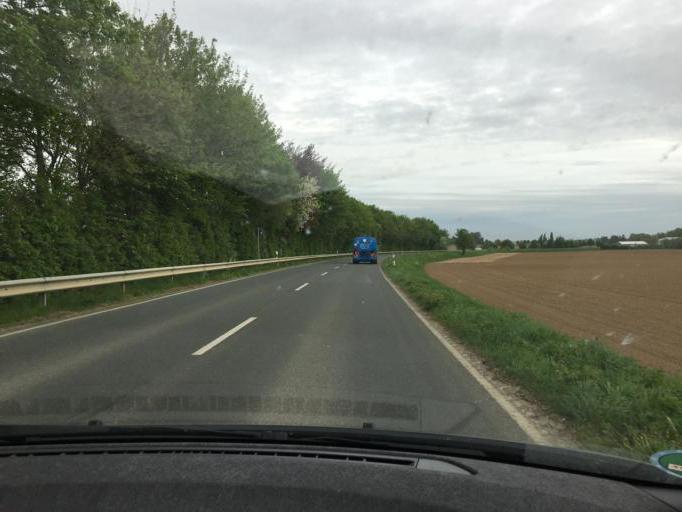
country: DE
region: North Rhine-Westphalia
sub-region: Regierungsbezirk Koln
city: Titz
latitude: 51.0435
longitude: 6.4299
